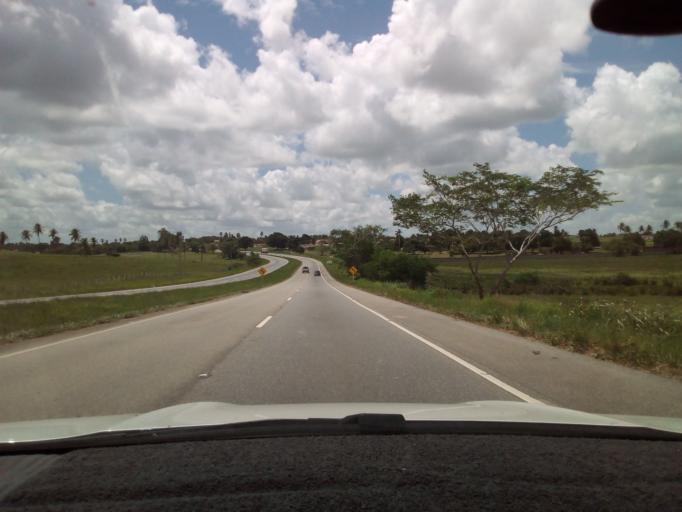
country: BR
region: Paraiba
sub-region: Pilar
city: Pilar
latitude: -7.1903
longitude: -35.2730
